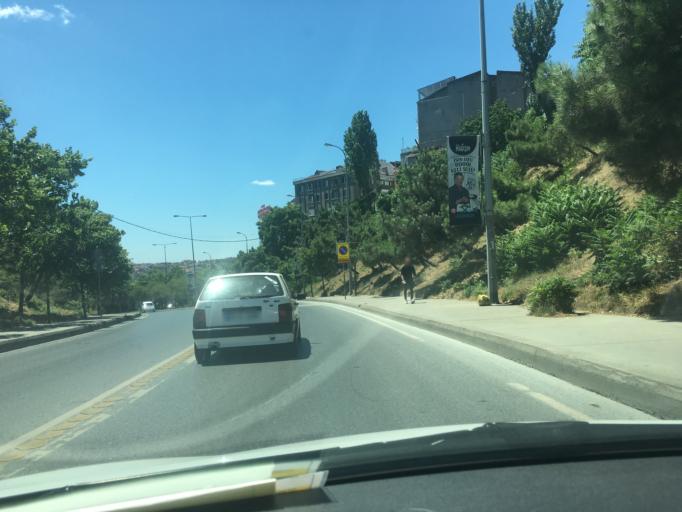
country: TR
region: Istanbul
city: Istanbul
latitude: 41.0516
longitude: 28.9470
